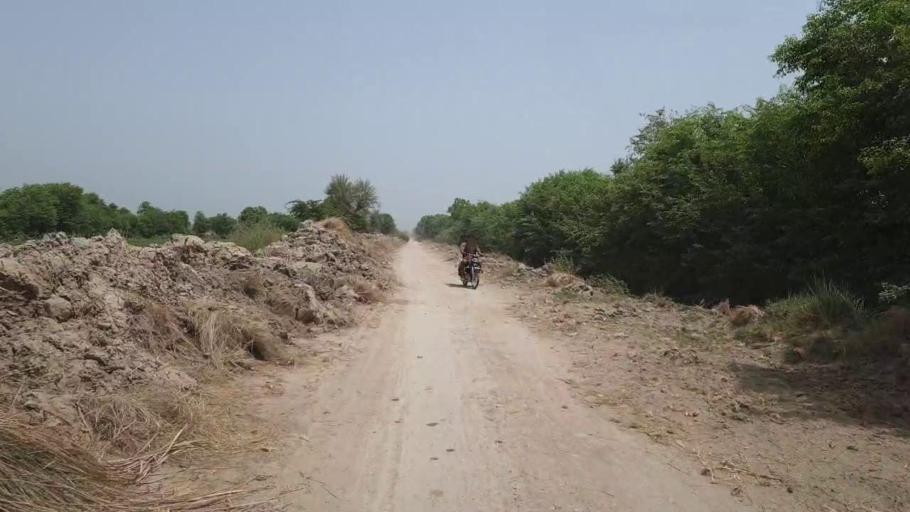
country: PK
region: Sindh
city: Nawabshah
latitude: 26.3178
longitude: 68.2990
